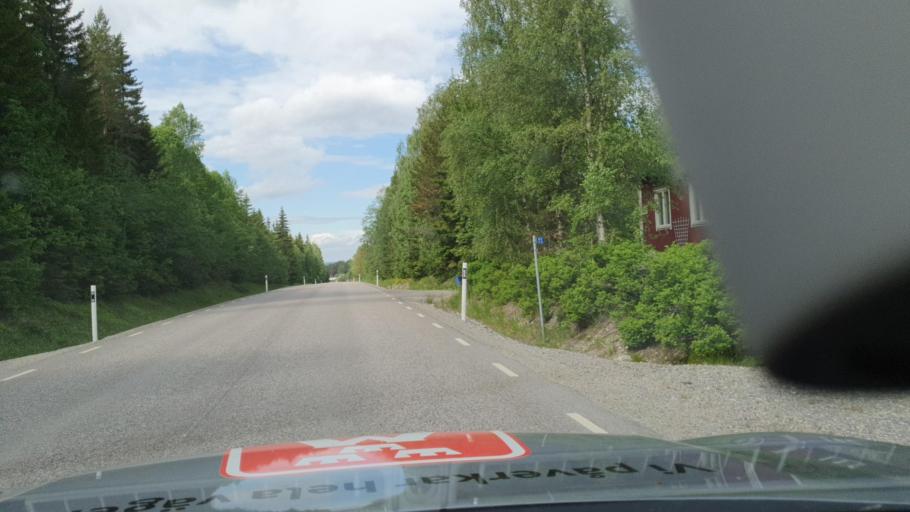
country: SE
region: Vaesternorrland
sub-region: Kramfors Kommun
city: Kramfors
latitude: 62.9198
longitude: 17.9496
